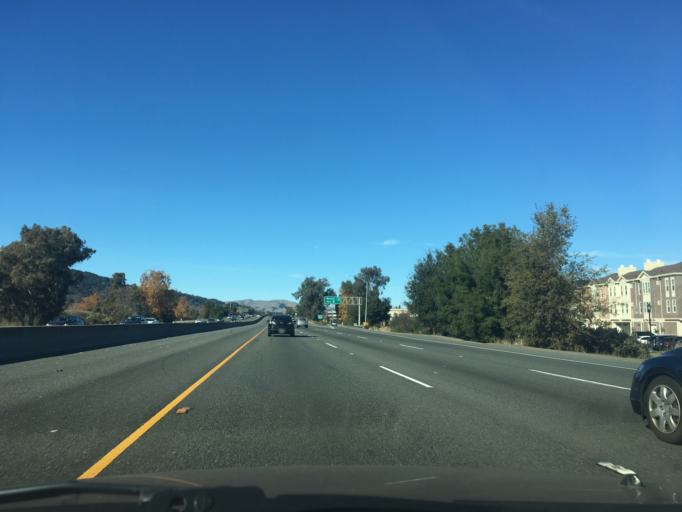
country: US
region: California
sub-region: Alameda County
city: Pleasanton
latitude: 37.6531
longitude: -121.8976
